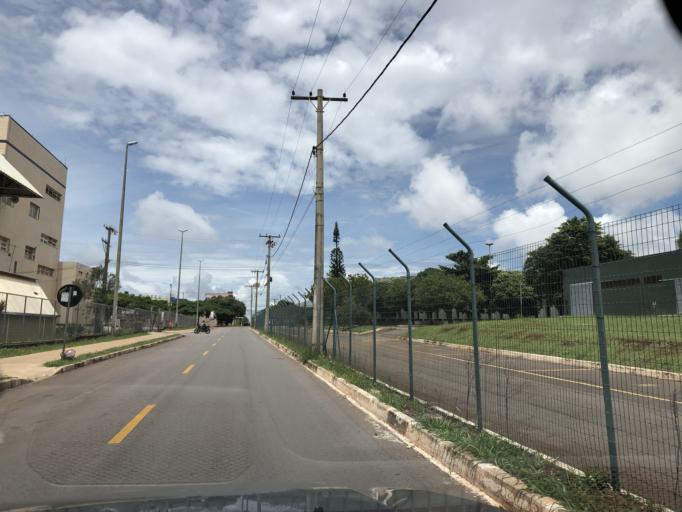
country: BR
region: Federal District
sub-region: Brasilia
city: Brasilia
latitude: -15.8190
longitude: -48.1021
